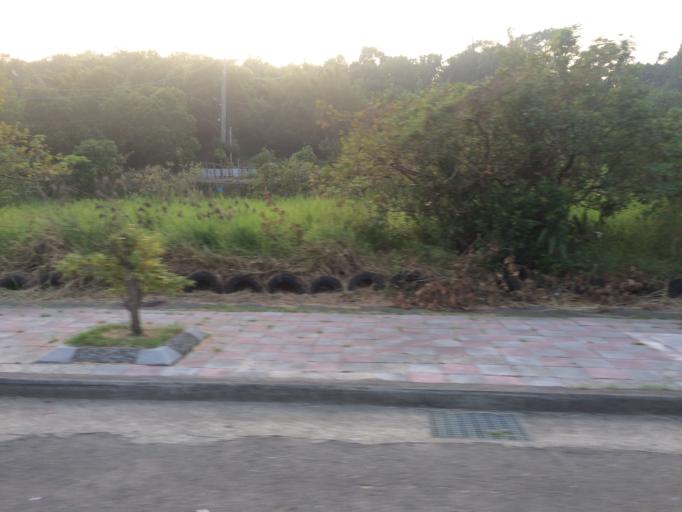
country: TW
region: Taiwan
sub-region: Hsinchu
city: Hsinchu
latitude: 24.7236
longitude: 120.9190
